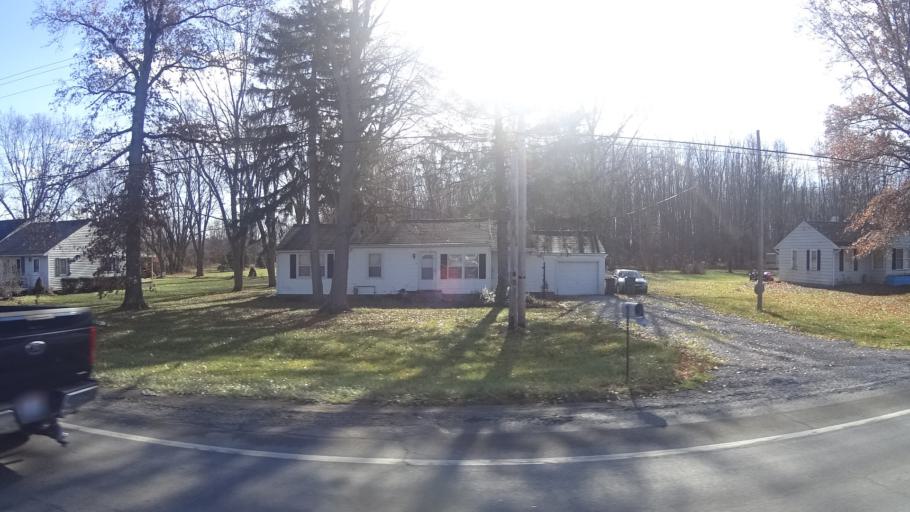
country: US
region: Ohio
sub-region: Lorain County
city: Eaton Estates
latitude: 41.3135
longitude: -81.9775
